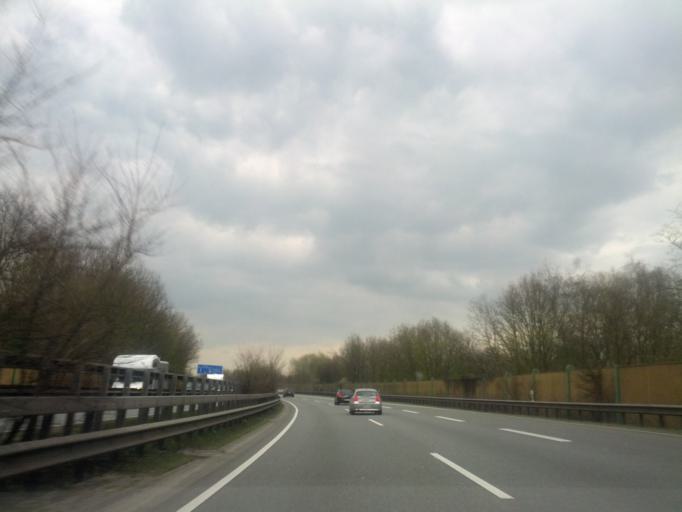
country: DE
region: Lower Saxony
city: Oldenburg
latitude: 53.1287
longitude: 8.1994
